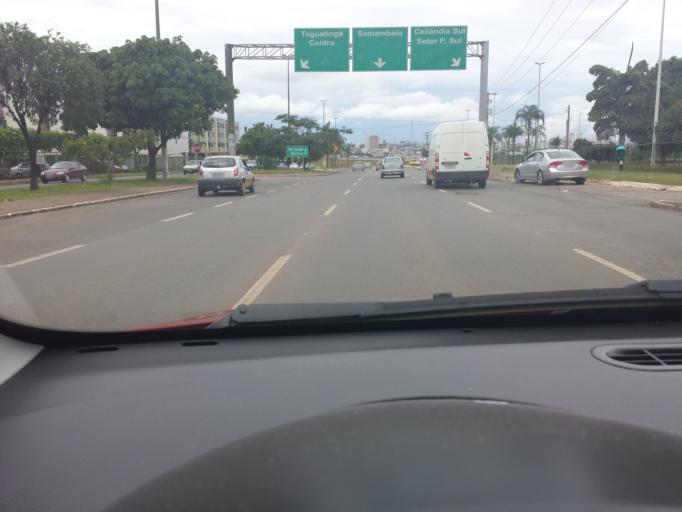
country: BR
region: Federal District
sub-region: Brasilia
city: Brasilia
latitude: -15.8327
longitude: -48.0774
